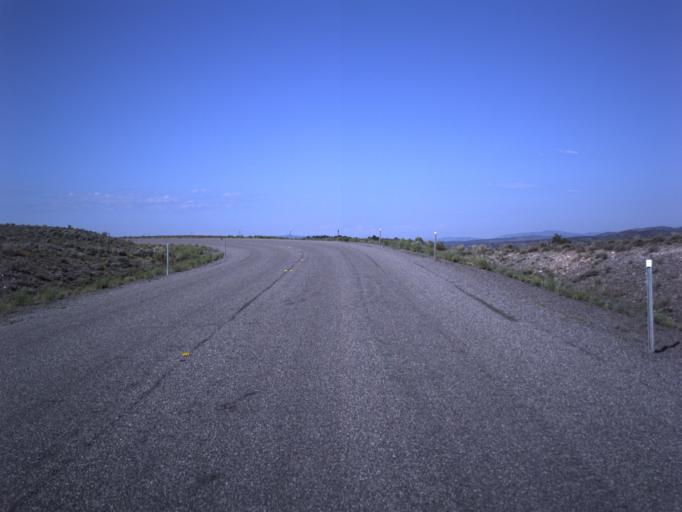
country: US
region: Utah
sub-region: Wayne County
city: Loa
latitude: 38.5086
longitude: -111.5277
